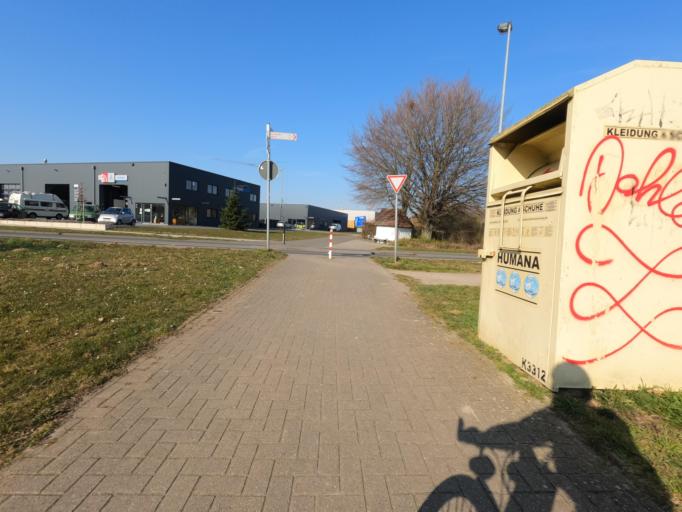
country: DE
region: North Rhine-Westphalia
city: Erkelenz
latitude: 51.0642
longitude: 6.3029
